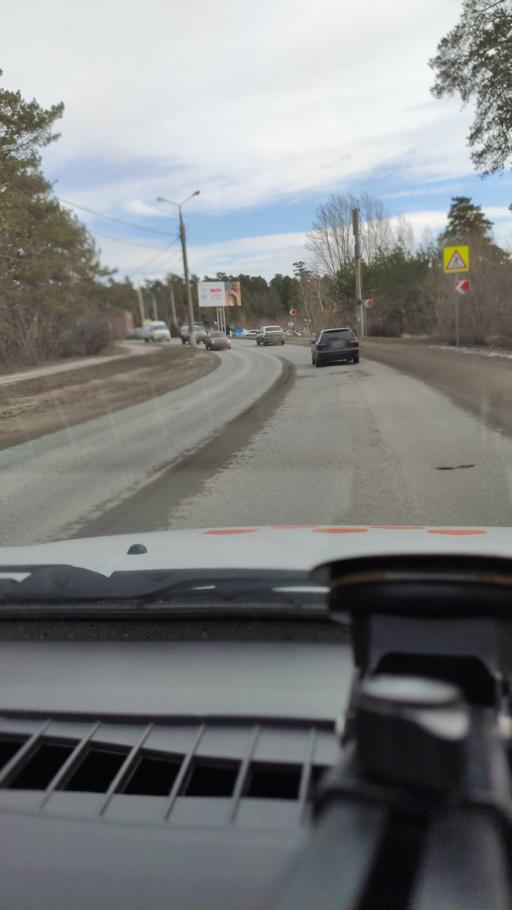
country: RU
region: Samara
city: Tol'yatti
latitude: 53.4752
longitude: 49.3467
